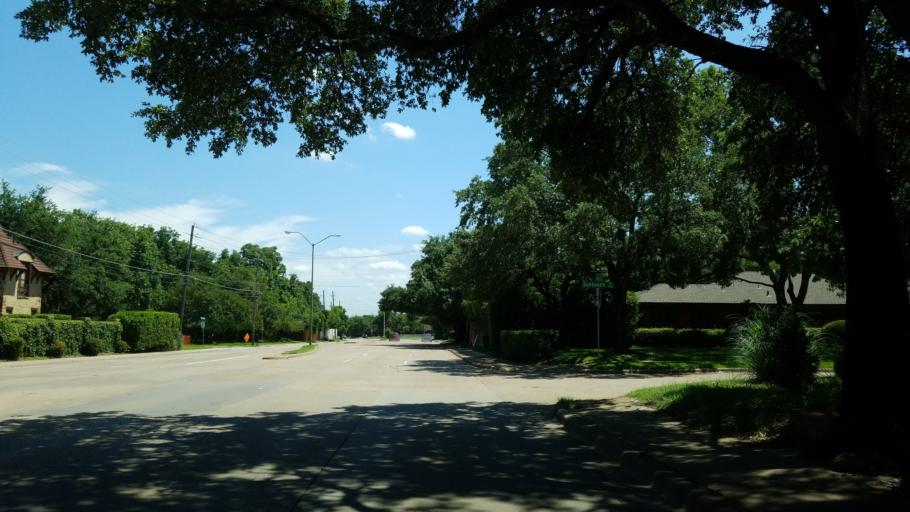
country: US
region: Texas
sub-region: Dallas County
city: University Park
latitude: 32.8720
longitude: -96.8386
